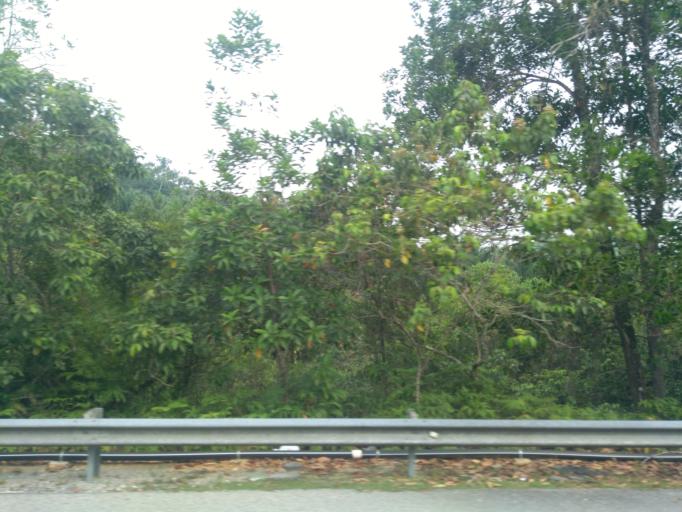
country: MY
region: Perak
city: Ipoh
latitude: 4.5548
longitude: 101.1672
